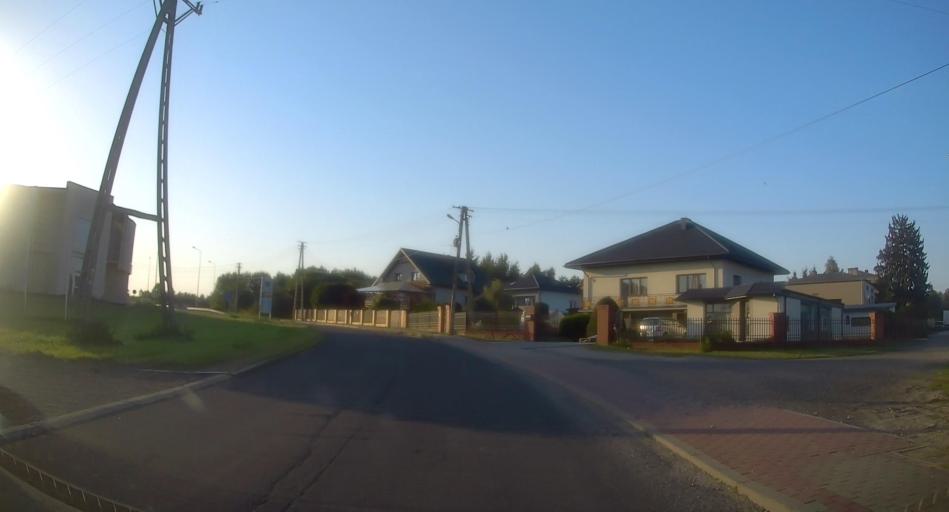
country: PL
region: Lodz Voivodeship
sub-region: Powiat skierniewicki
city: Kowiesy
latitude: 51.8909
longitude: 20.4243
